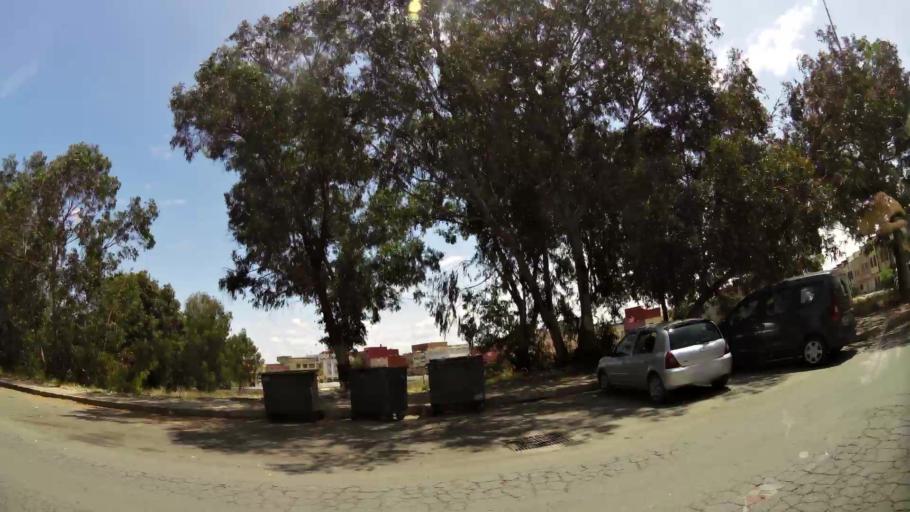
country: MA
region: Gharb-Chrarda-Beni Hssen
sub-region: Kenitra Province
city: Kenitra
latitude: 34.2618
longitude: -6.6125
